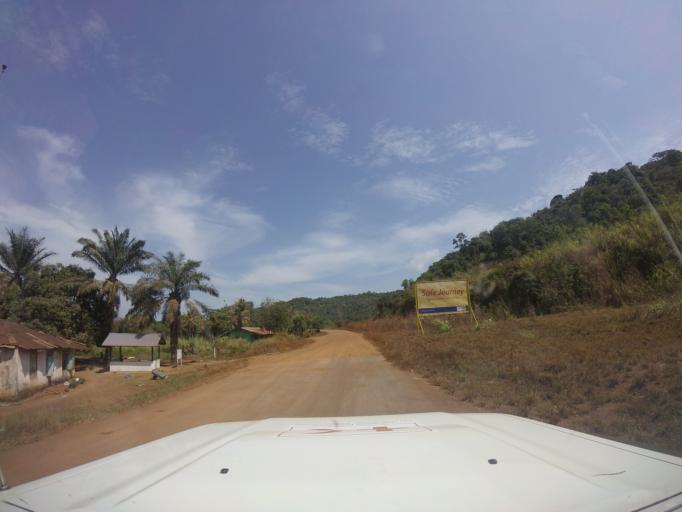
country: LR
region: Grand Cape Mount
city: Robertsport
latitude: 6.7515
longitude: -11.3624
